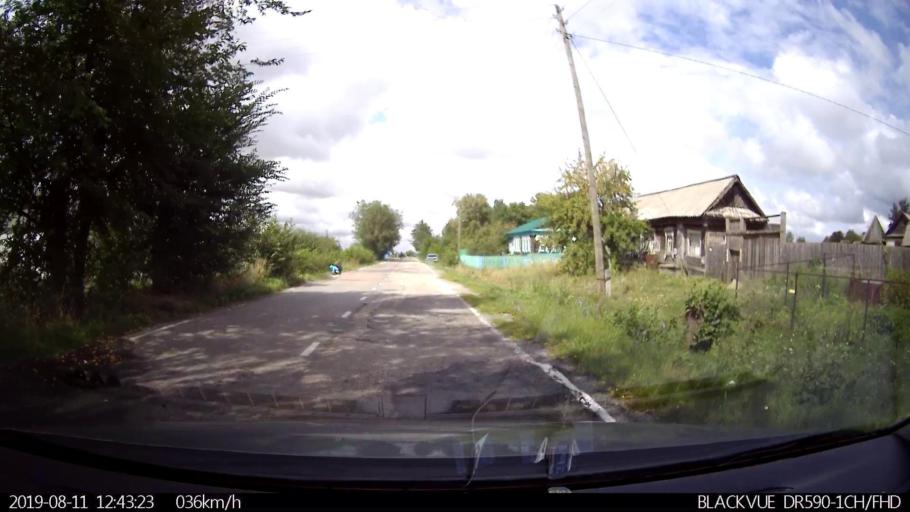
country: RU
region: Ulyanovsk
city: Ignatovka
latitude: 53.8506
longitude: 47.7432
